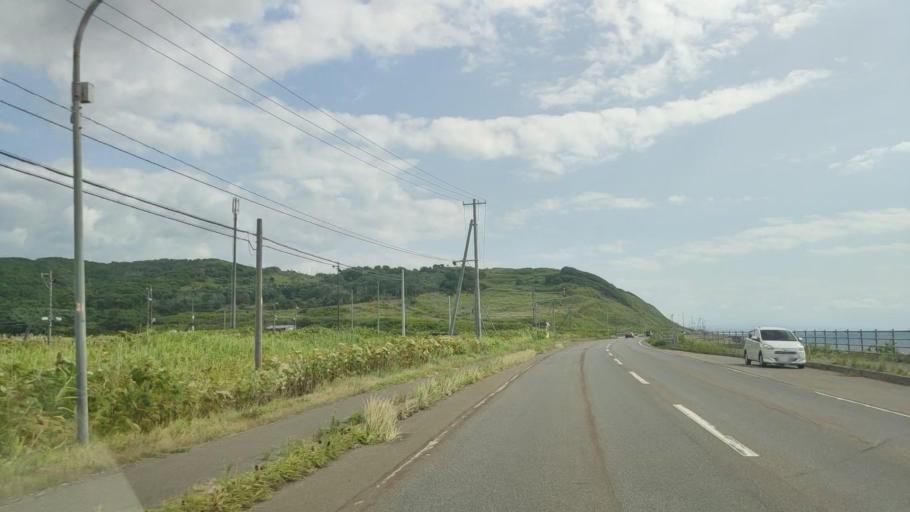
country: JP
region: Hokkaido
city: Rumoi
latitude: 44.1029
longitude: 141.6604
